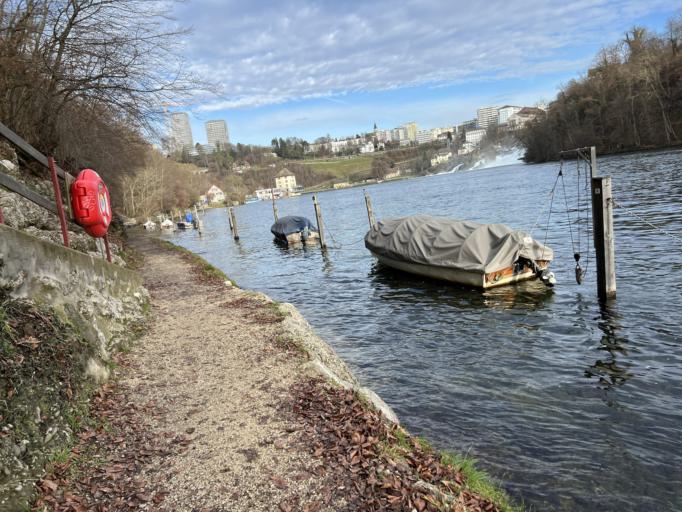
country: CH
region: Schaffhausen
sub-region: Bezirk Schaffhausen
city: Neuhausen
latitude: 47.6747
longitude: 8.6095
